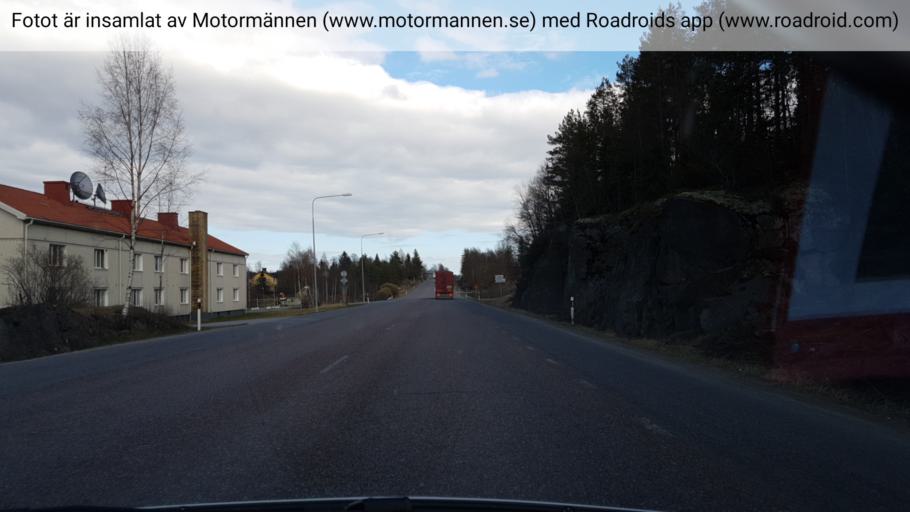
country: SE
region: Vaesternorrland
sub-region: Kramfors Kommun
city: Kramfors
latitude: 62.9083
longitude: 17.8165
